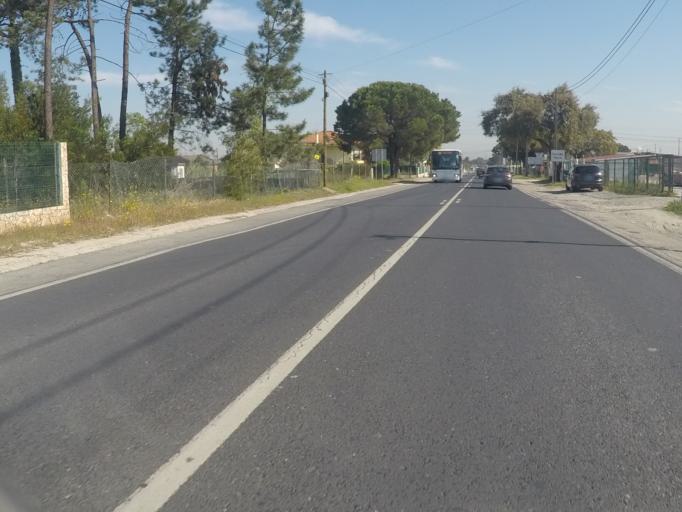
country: PT
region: Setubal
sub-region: Seixal
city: Arrentela
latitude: 38.5551
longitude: -9.1007
